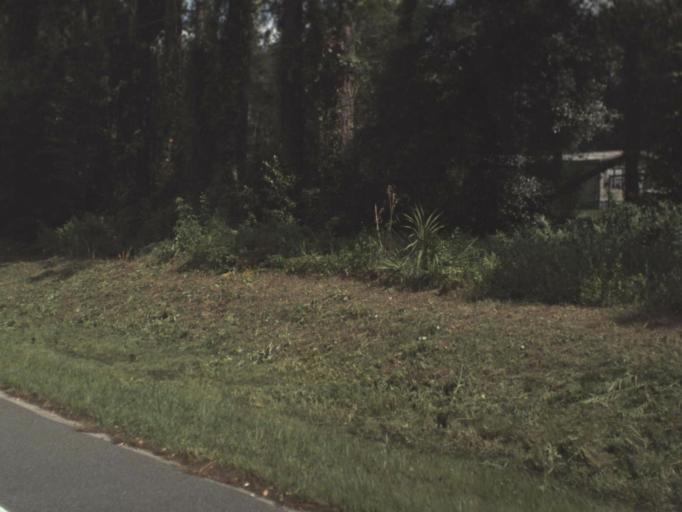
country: US
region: Florida
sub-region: Putnam County
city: Interlachen
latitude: 29.7254
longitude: -81.8394
